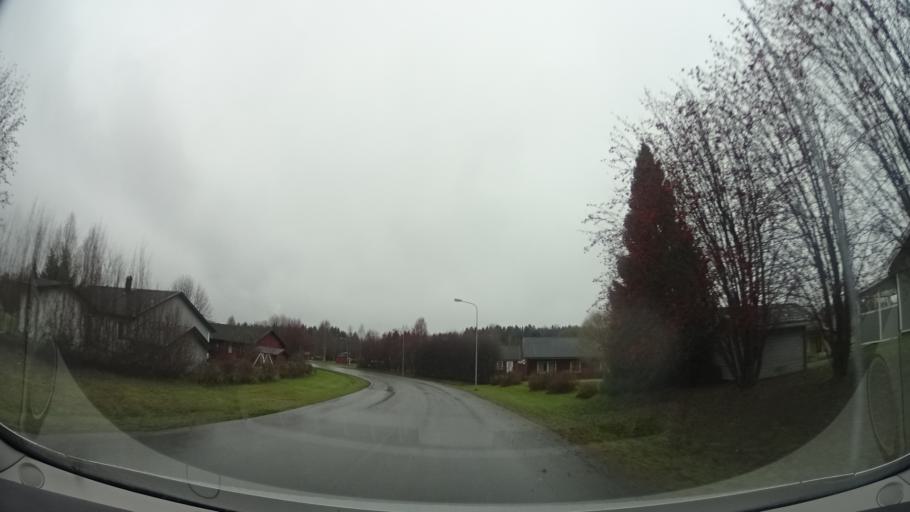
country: SE
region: Vaesterbotten
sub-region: Skelleftea Kommun
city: Soedra Bergsbyn
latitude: 64.7557
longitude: 21.0380
